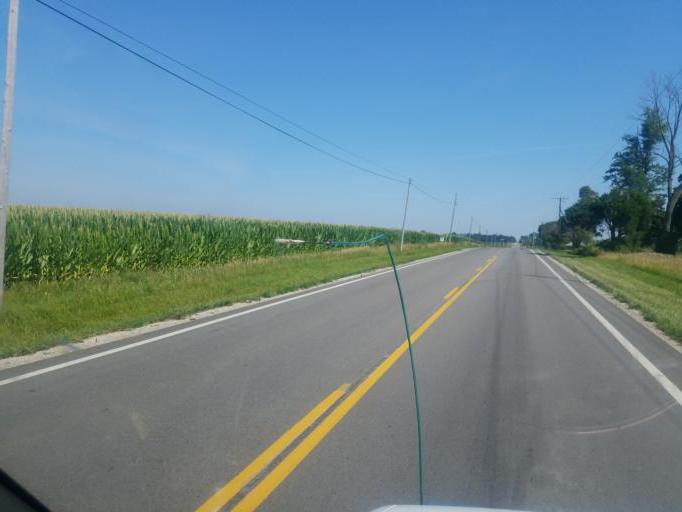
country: US
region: Ohio
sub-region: Union County
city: Marysville
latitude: 40.2919
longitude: -83.3794
